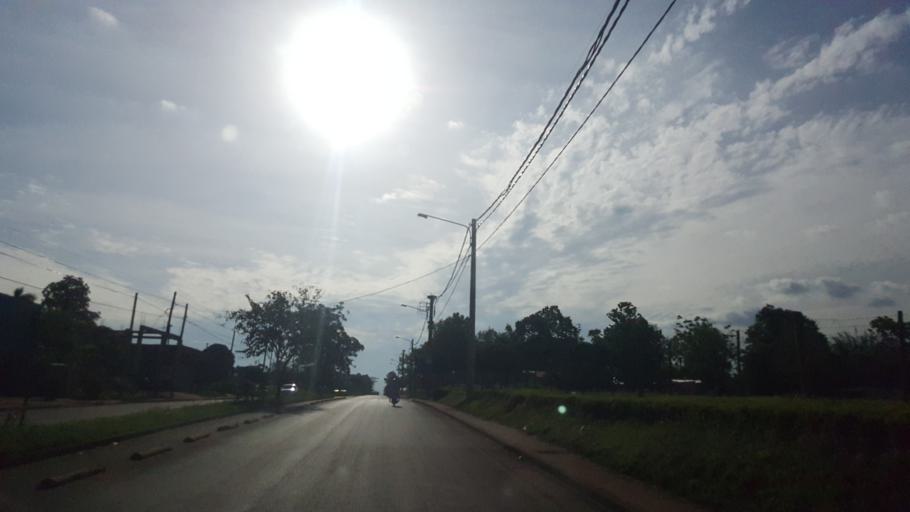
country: AR
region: Misiones
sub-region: Departamento de Capital
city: Posadas
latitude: -27.4270
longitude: -55.9203
